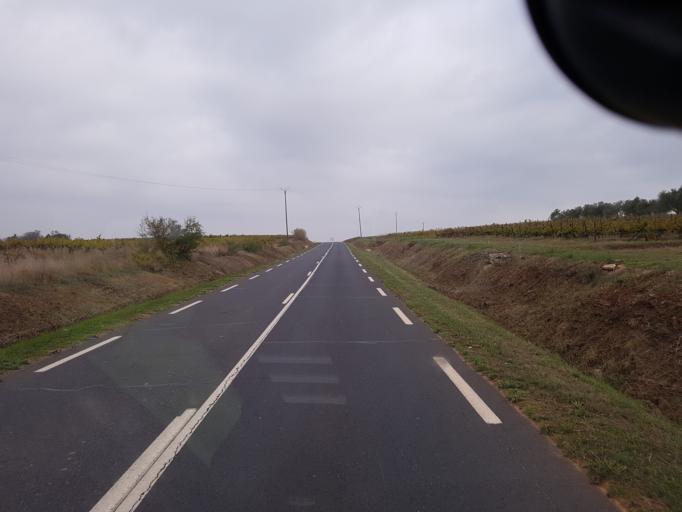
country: FR
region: Languedoc-Roussillon
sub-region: Departement de l'Herault
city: Marseillan
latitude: 43.3711
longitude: 3.5326
